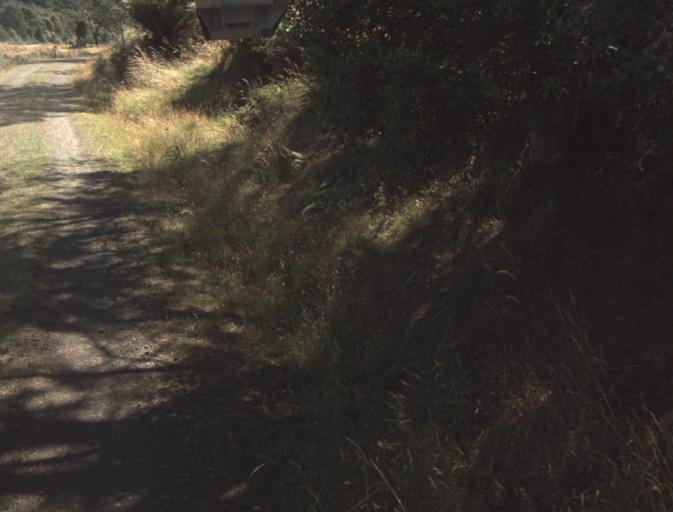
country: AU
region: Tasmania
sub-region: Dorset
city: Scottsdale
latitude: -41.3514
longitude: 147.4415
